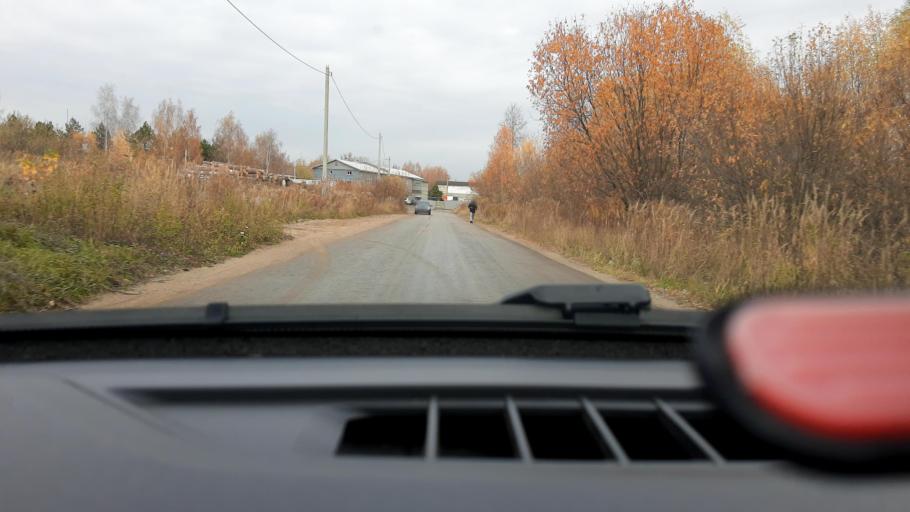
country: RU
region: Nizjnij Novgorod
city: Gorbatovka
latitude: 56.3182
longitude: 43.8463
